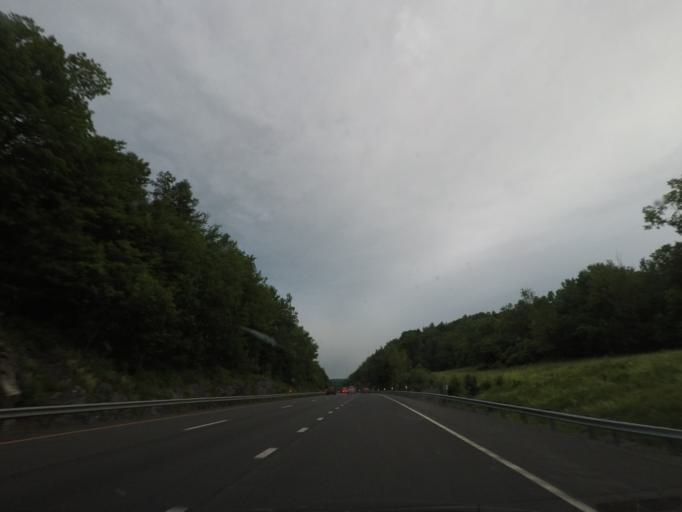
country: US
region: New York
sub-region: Columbia County
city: Chatham
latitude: 42.4261
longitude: -73.5509
